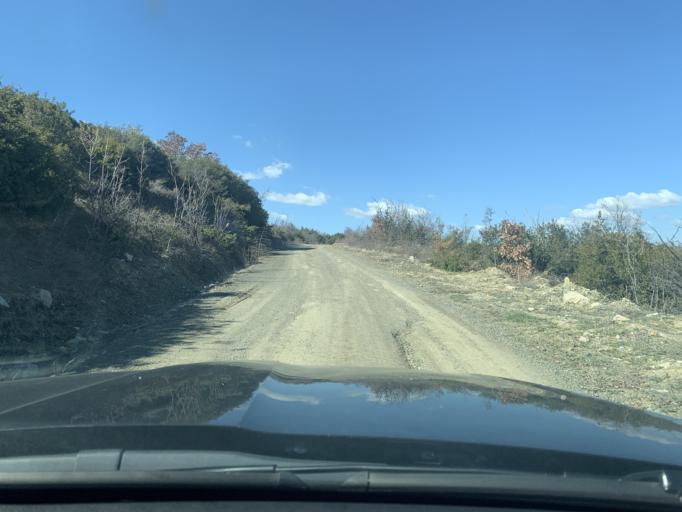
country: MK
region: Demir Kapija
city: Demir Kapija
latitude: 41.4119
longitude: 22.2250
